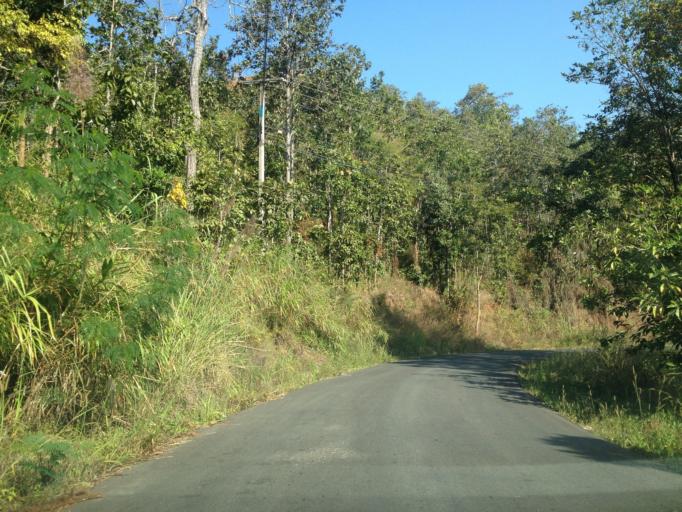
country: TH
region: Mae Hong Son
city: Ban Huai I Huak
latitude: 18.1408
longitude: 98.2181
